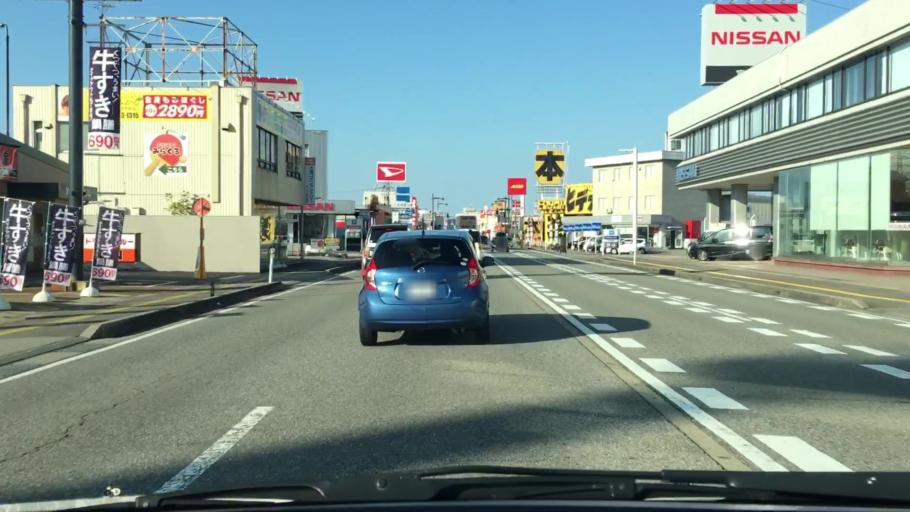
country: JP
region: Toyama
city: Toyama-shi
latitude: 36.6961
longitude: 137.2448
